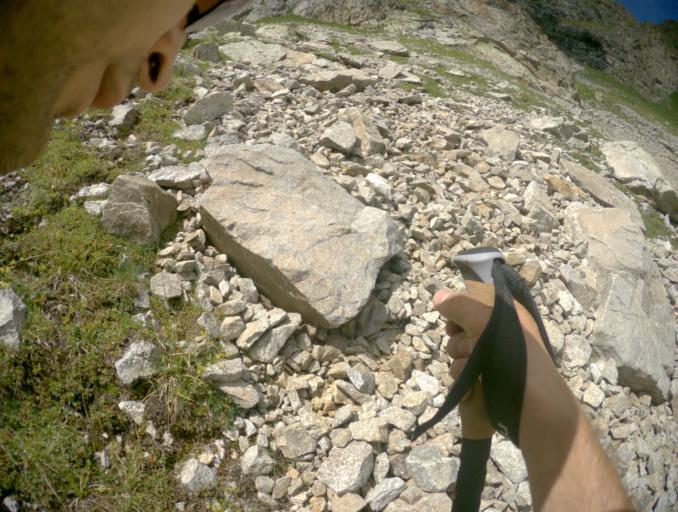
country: RU
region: Karachayevo-Cherkesiya
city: Uchkulan
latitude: 43.3254
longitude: 42.0898
